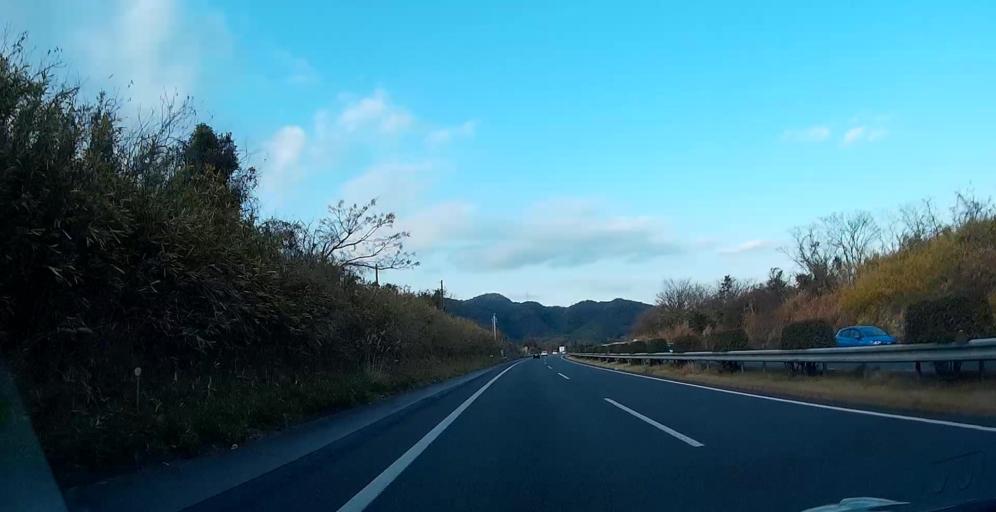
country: JP
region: Kumamoto
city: Matsubase
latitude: 32.6652
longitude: 130.7123
